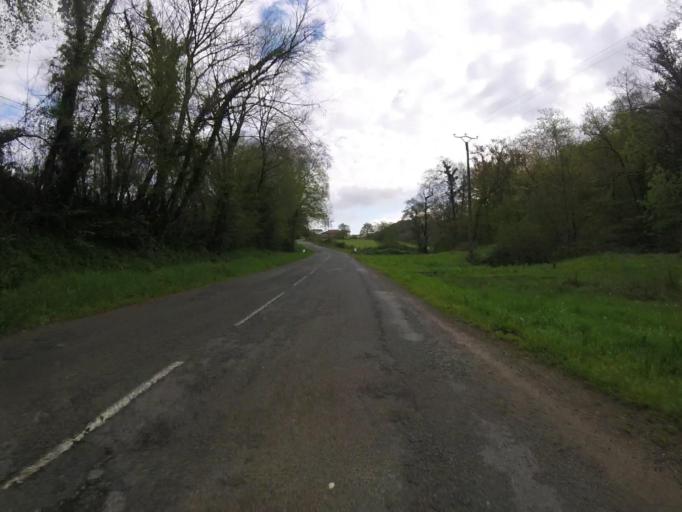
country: FR
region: Aquitaine
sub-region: Departement des Pyrenees-Atlantiques
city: Sare
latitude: 43.2953
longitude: -1.5919
